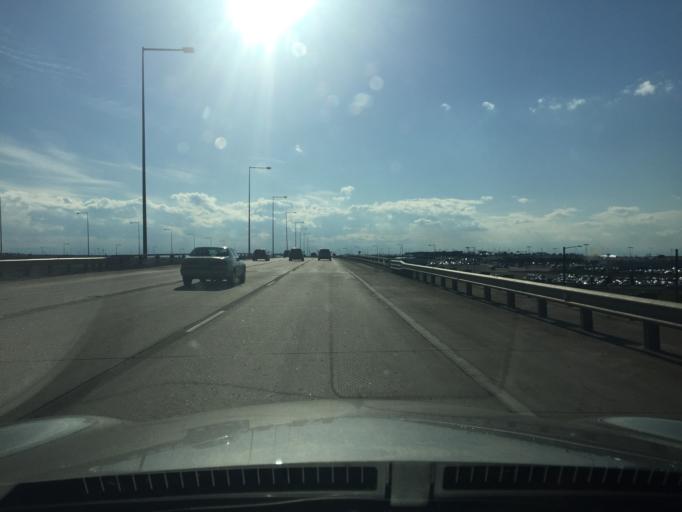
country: US
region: Colorado
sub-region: Weld County
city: Lochbuie
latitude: 39.8343
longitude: -104.6922
